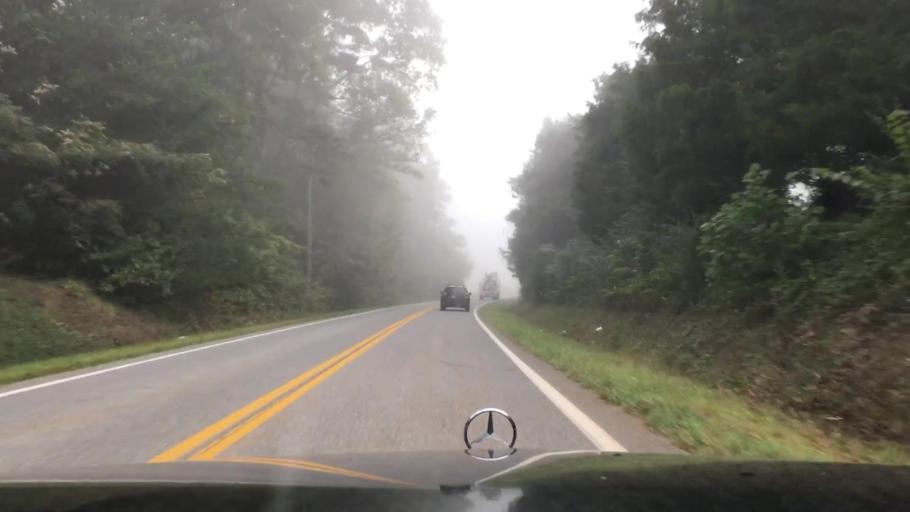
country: US
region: Virginia
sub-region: Campbell County
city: Timberlake
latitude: 37.2239
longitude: -79.2871
